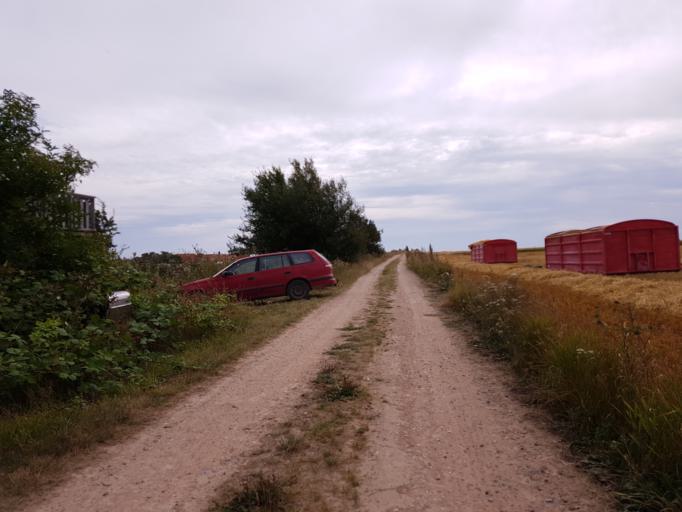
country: DK
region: Zealand
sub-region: Guldborgsund Kommune
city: Nykobing Falster
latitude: 54.5950
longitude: 11.9270
